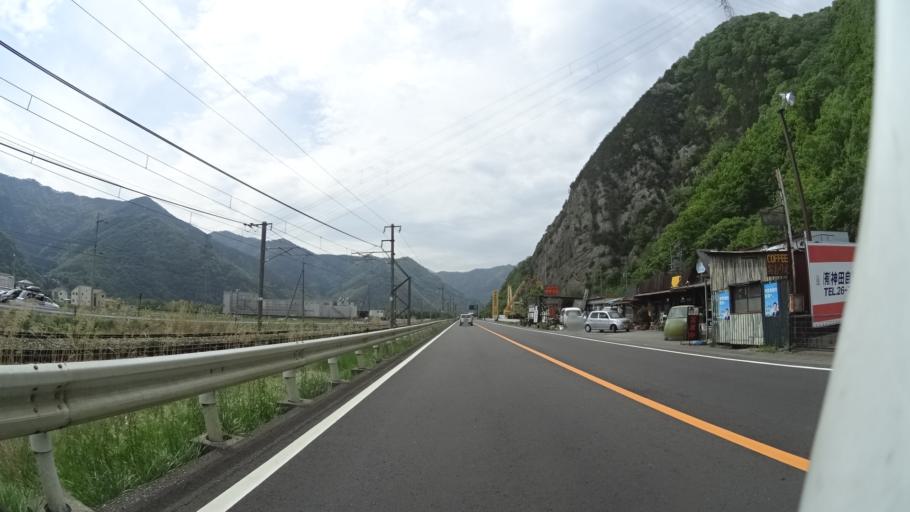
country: JP
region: Nagano
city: Ueda
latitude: 36.4205
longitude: 138.2002
